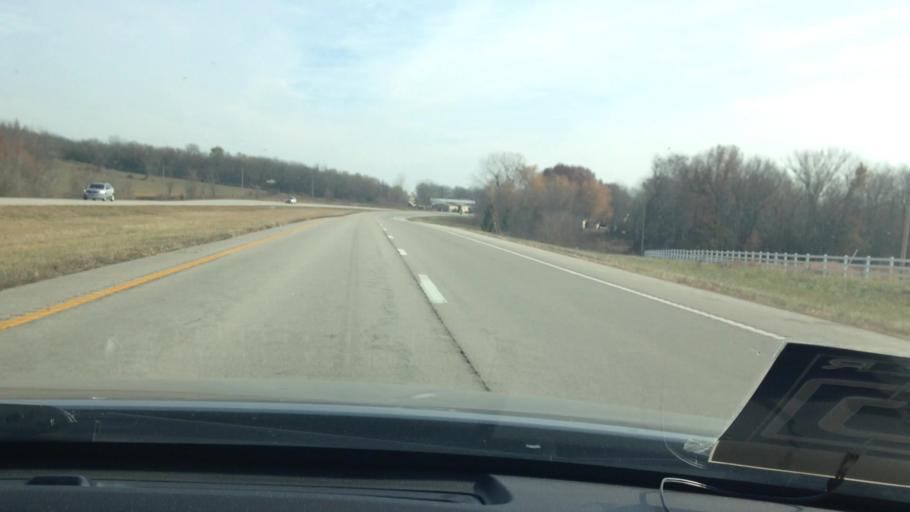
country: US
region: Missouri
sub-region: Cass County
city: Harrisonville
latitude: 38.6172
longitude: -94.3363
